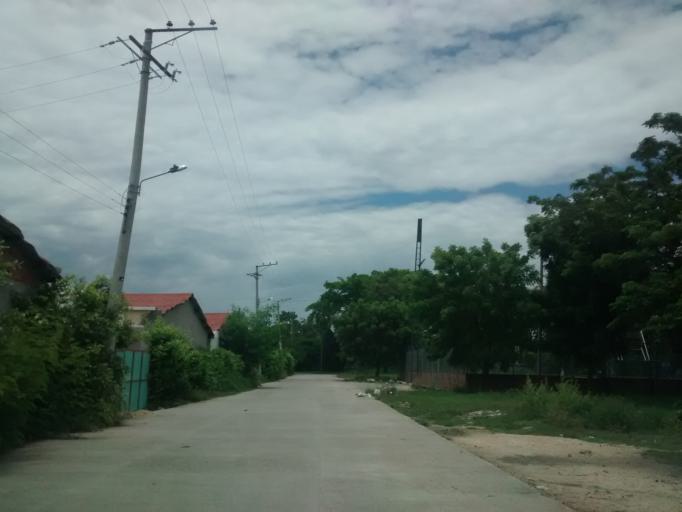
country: CO
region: Cundinamarca
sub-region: Girardot
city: Girardot City
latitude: 4.3091
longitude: -74.8093
